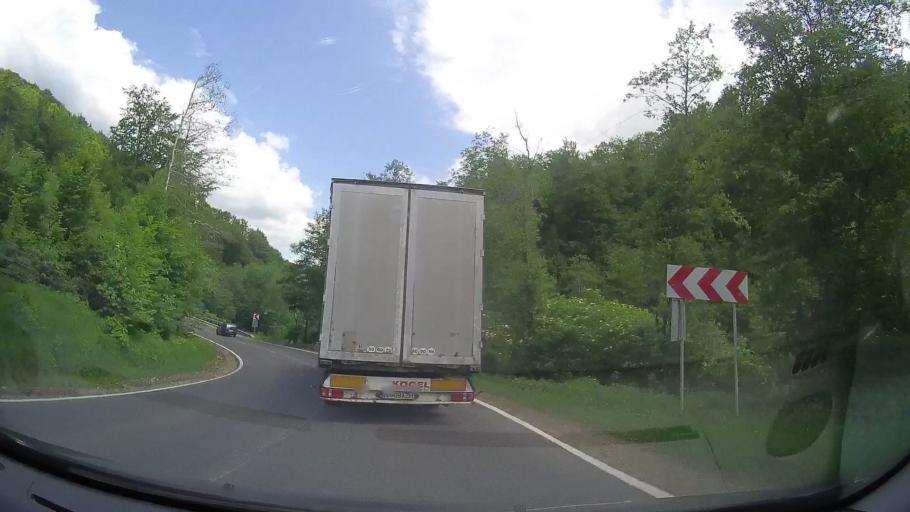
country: RO
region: Prahova
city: Maneciu
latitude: 45.3780
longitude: 25.9302
